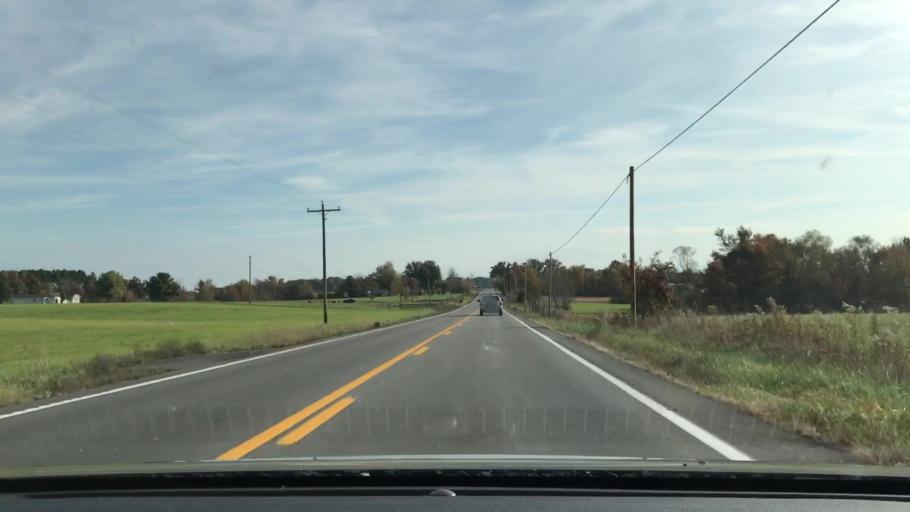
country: US
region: Tennessee
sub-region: Fentress County
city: Grimsley
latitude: 36.1804
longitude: -85.0458
